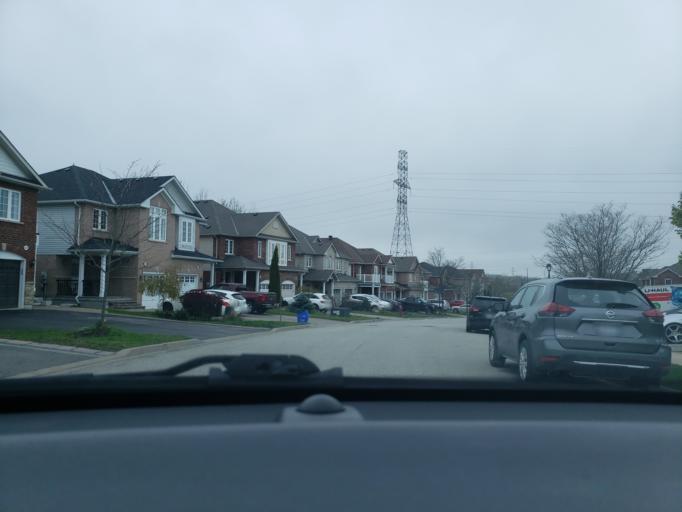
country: CA
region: Ontario
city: Newmarket
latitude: 44.0334
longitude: -79.4568
